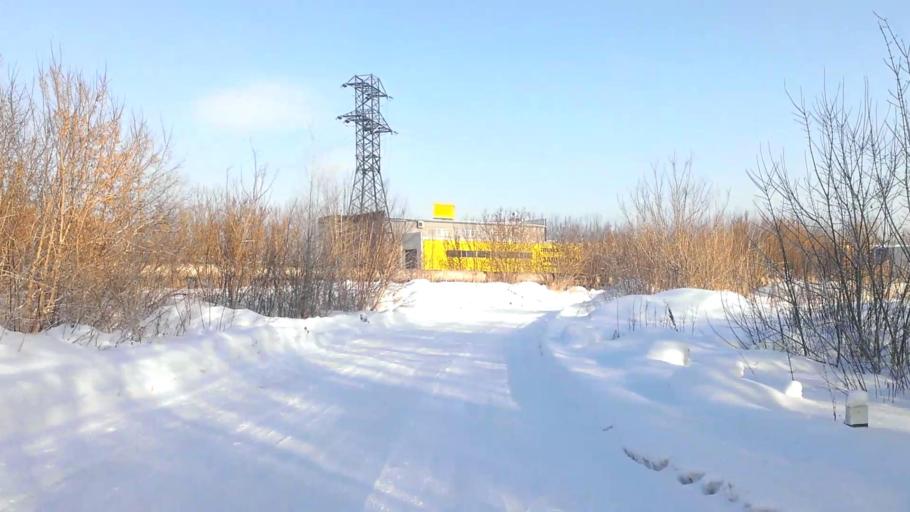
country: RU
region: Altai Krai
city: Novosilikatnyy
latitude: 53.3465
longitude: 83.6293
